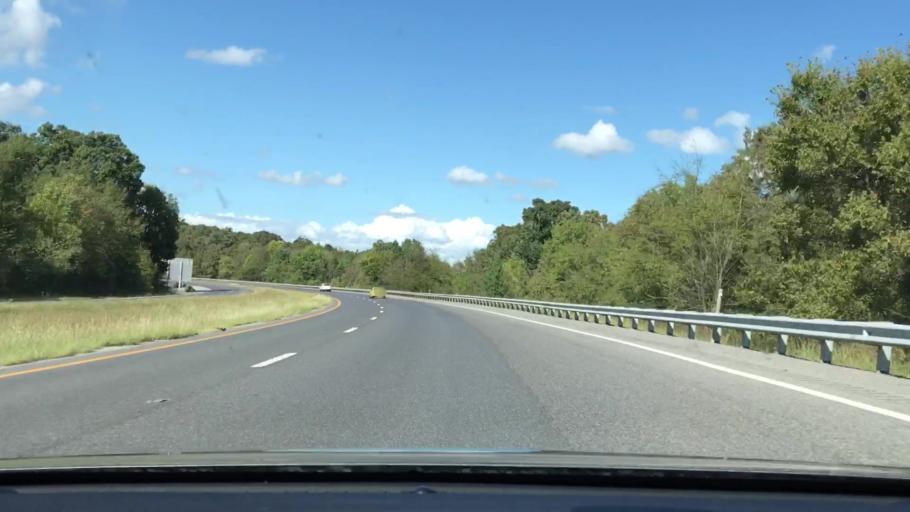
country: US
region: Kentucky
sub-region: Marshall County
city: Benton
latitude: 36.9324
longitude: -88.3430
